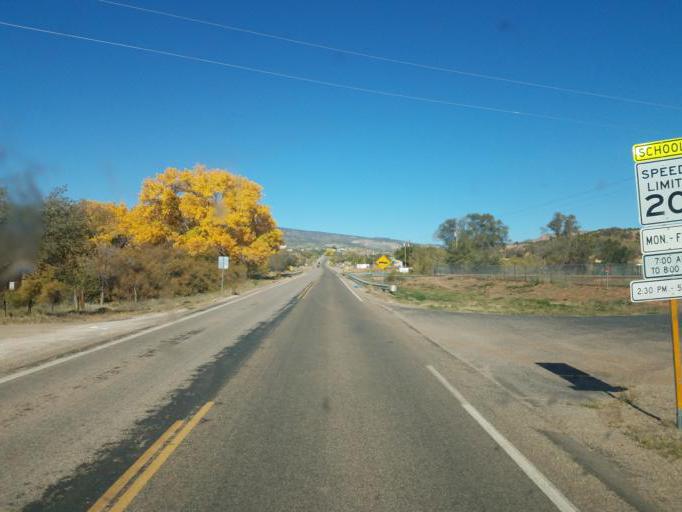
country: US
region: New Mexico
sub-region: Sandoval County
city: Jemez Pueblo
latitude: 35.6513
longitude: -106.7314
